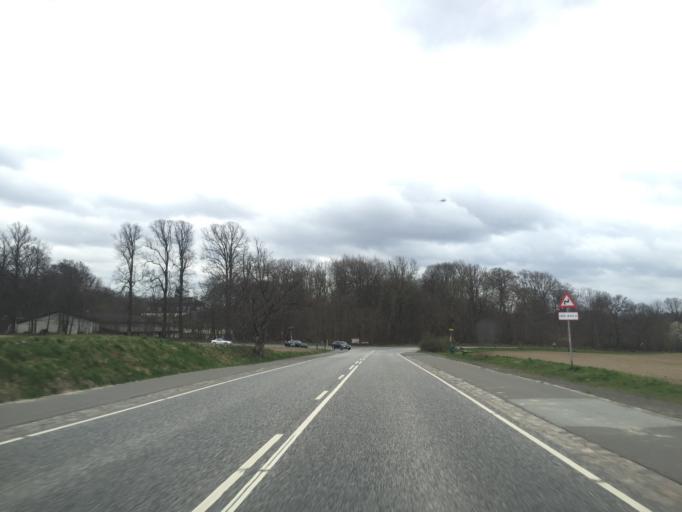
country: DK
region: Capital Region
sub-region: Rudersdal Kommune
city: Holte
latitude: 55.7858
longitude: 12.4513
